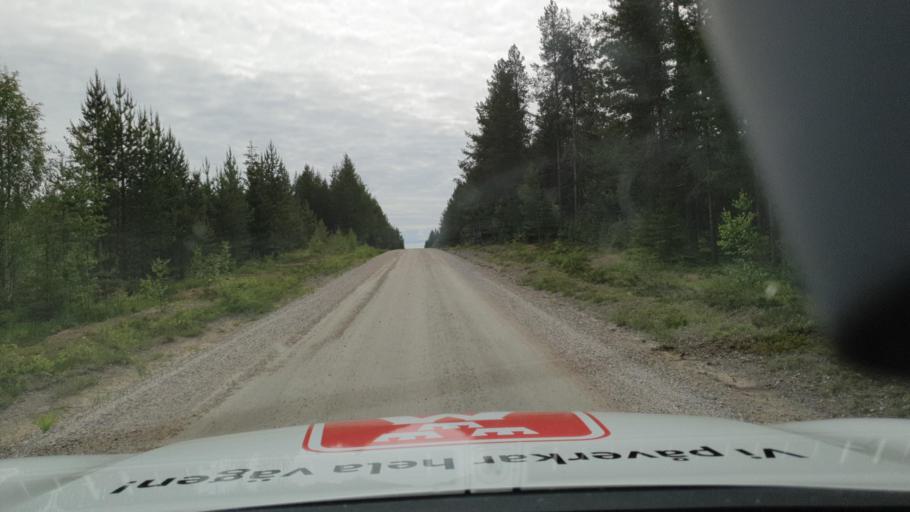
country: SE
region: Vaesterbotten
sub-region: Skelleftea Kommun
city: Forsbacka
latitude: 64.6473
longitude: 20.4511
